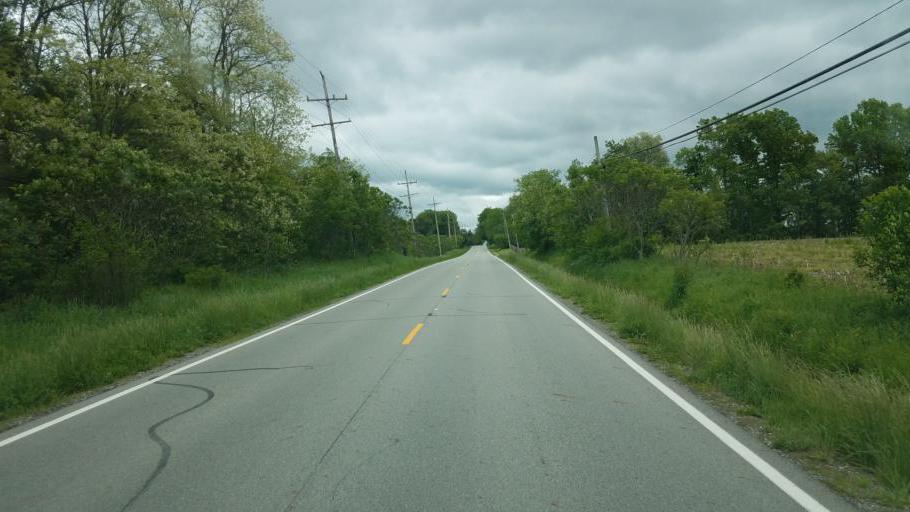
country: US
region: Ohio
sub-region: Geauga County
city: Burton
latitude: 41.3966
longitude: -81.1717
